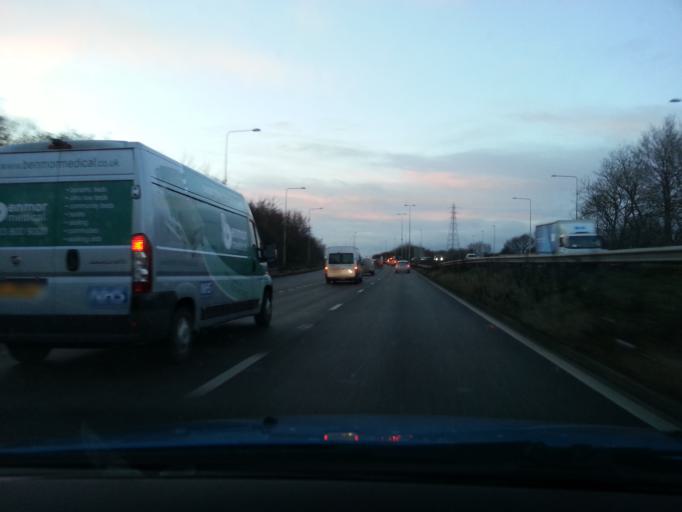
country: GB
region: England
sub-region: Gateshead
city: Lamesley
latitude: 54.9092
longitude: -1.5763
